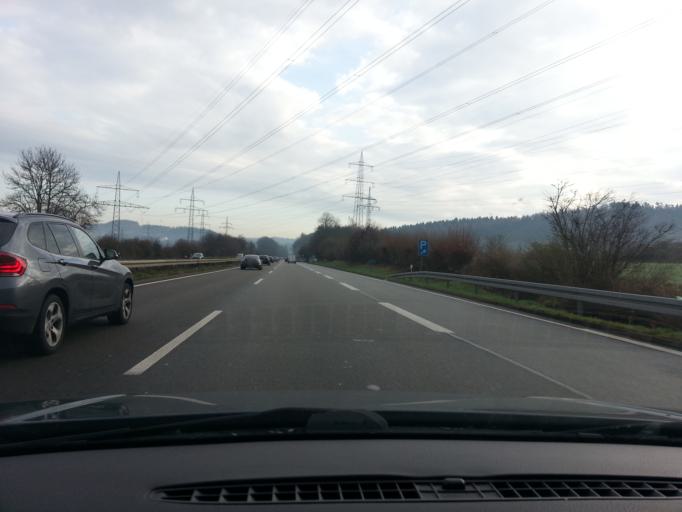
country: DE
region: Saarland
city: Kirkel
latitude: 49.3008
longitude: 7.2836
